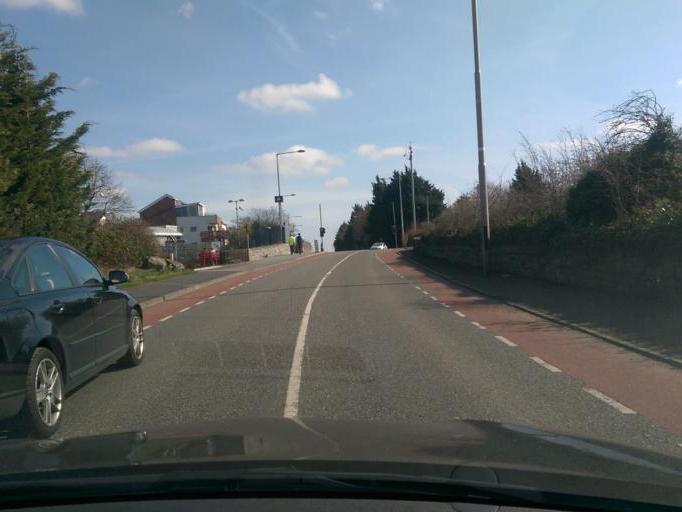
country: IE
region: Leinster
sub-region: Kildare
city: Leixlip
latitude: 53.3700
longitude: -6.5082
